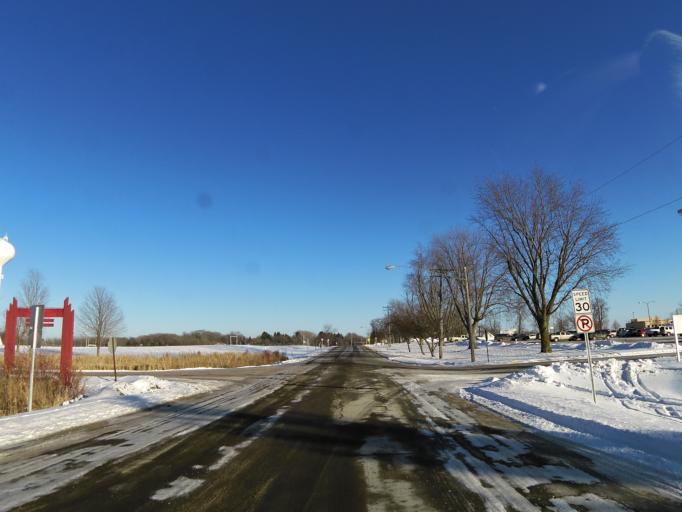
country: US
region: Minnesota
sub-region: Hennepin County
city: Mound
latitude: 44.9567
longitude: -93.6734
